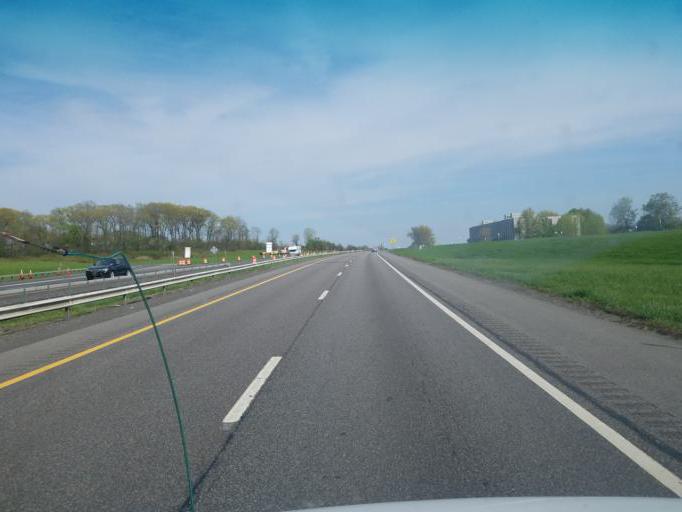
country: US
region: New York
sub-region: Onondaga County
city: Galeville
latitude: 43.1020
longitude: -76.1814
